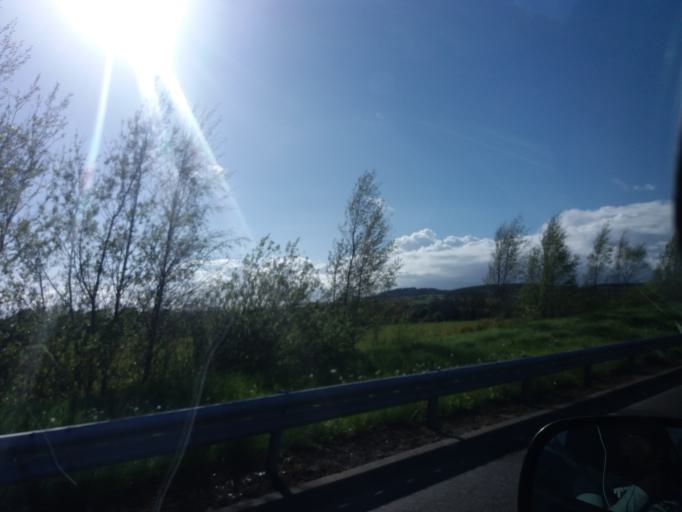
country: IE
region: Munster
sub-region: Waterford
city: Waterford
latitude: 52.3332
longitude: -7.1569
